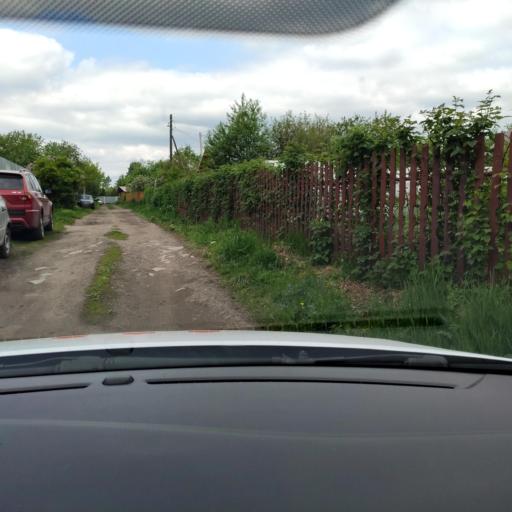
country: RU
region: Tatarstan
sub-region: Gorod Kazan'
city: Kazan
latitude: 55.8696
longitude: 49.1053
